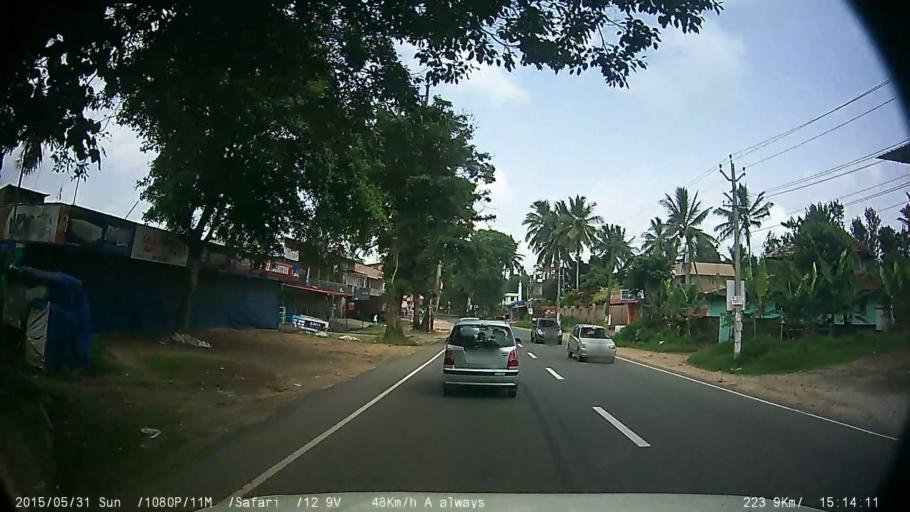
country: IN
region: Kerala
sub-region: Wayanad
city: Panamaram
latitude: 11.6599
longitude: 76.2440
